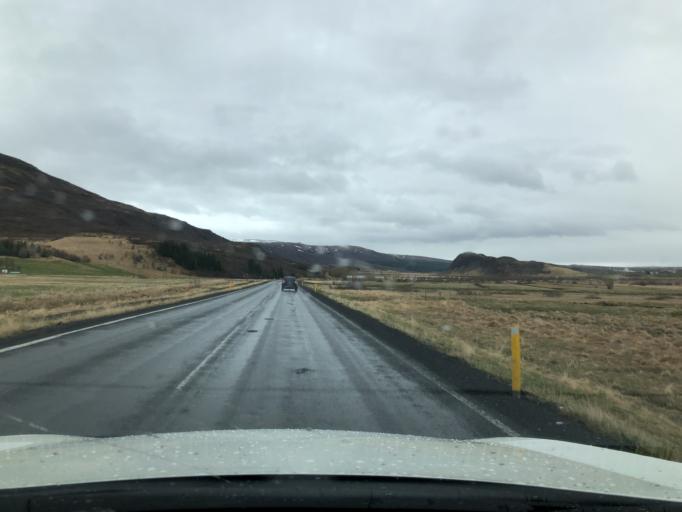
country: IS
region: South
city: Selfoss
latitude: 64.2985
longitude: -20.3321
